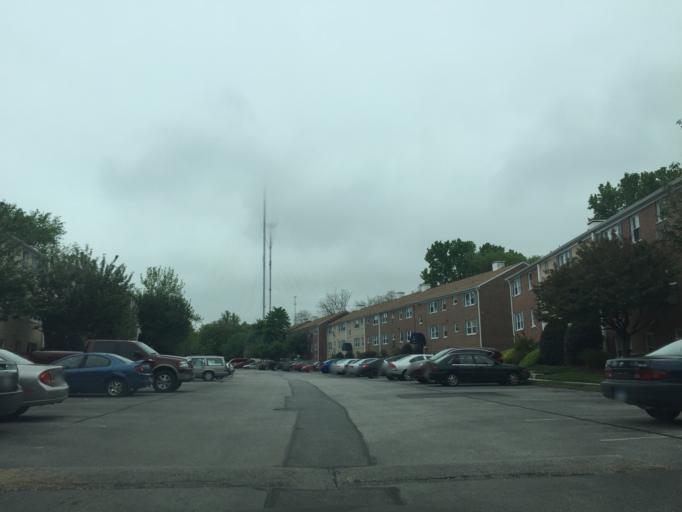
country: US
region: Maryland
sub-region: City of Baltimore
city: Baltimore
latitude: 39.3440
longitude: -76.6453
